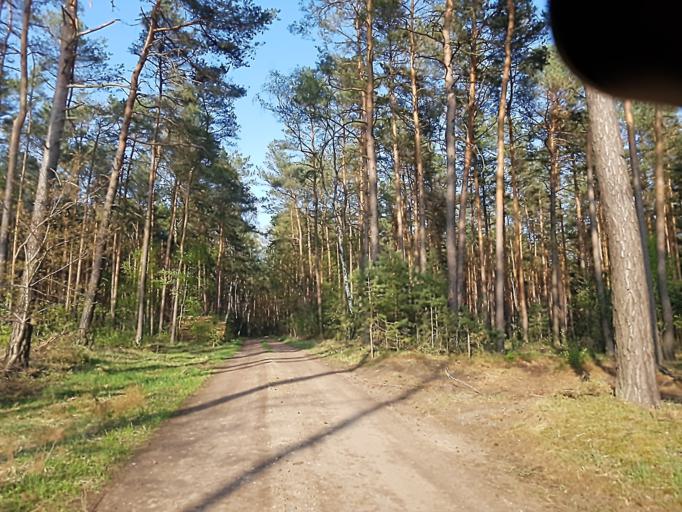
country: DE
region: Brandenburg
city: Schilda
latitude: 51.5589
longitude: 13.3804
